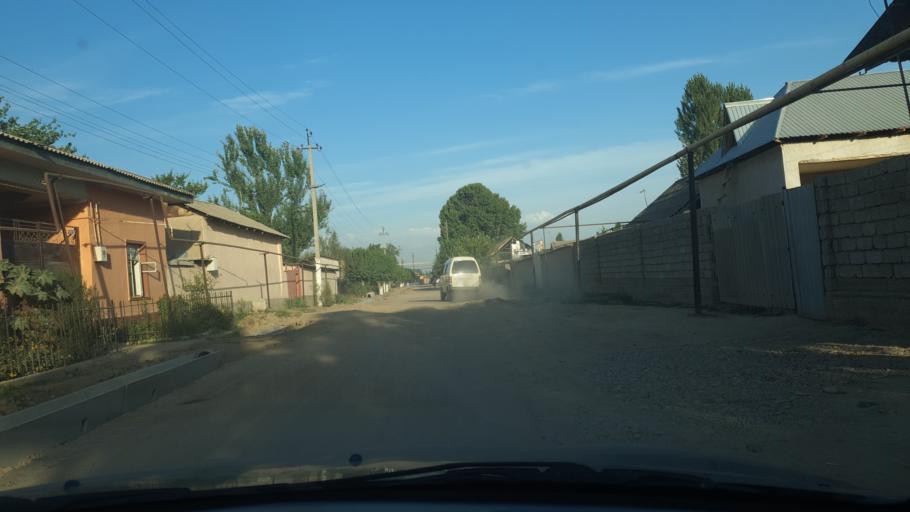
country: UZ
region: Toshkent
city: Tuytepa
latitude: 41.1041
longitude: 69.3989
